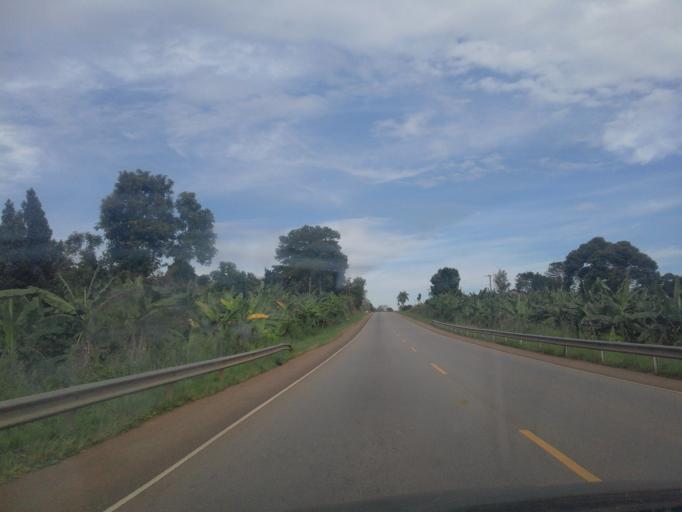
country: UG
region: Central Region
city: Masaka
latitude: -0.3464
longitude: 31.6157
